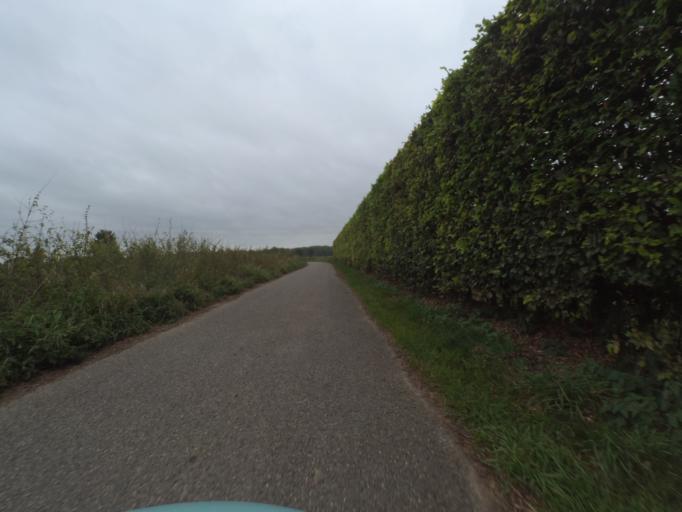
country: NL
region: Gelderland
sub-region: Gemeente Tiel
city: Tiel
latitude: 51.9048
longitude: 5.3798
